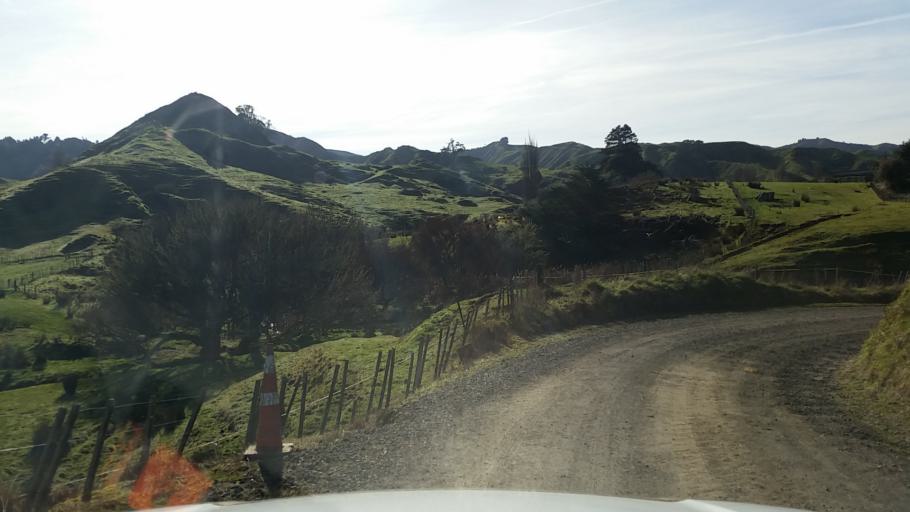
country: NZ
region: Taranaki
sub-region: South Taranaki District
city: Eltham
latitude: -39.3116
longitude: 174.5377
